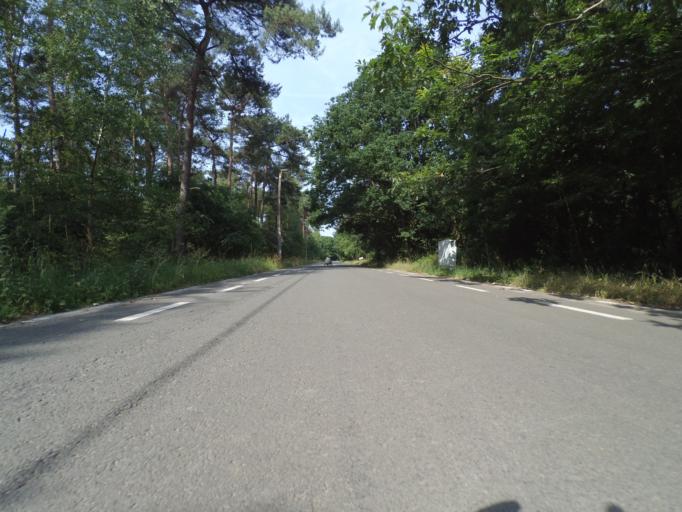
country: BE
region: Flanders
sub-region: Provincie Antwerpen
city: Stabroek
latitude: 51.3554
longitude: 4.3578
